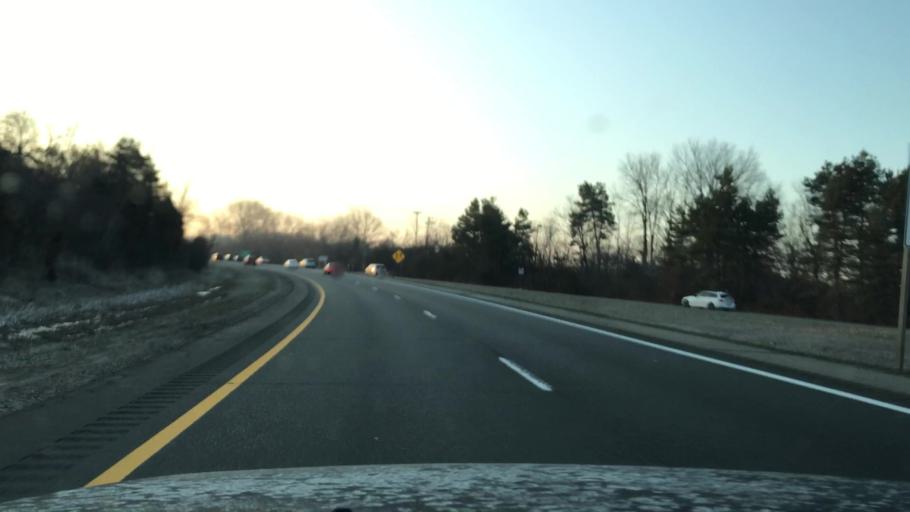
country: US
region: Michigan
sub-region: Kent County
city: East Grand Rapids
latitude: 42.9759
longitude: -85.6026
